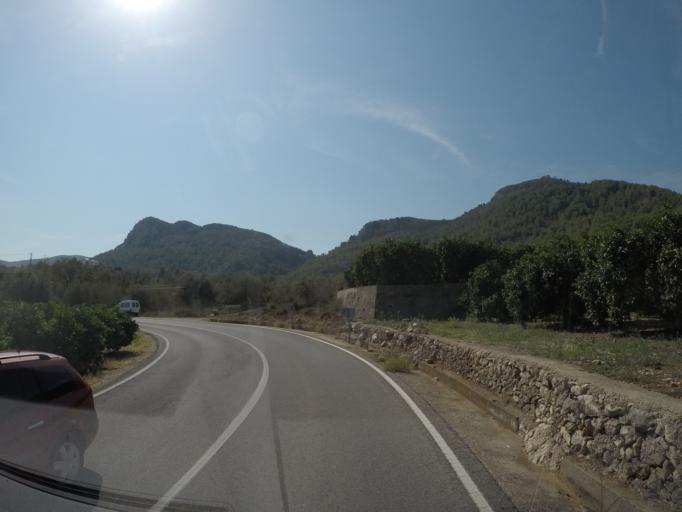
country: ES
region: Valencia
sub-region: Provincia de Alicante
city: Orba
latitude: 38.7809
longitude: -0.0738
